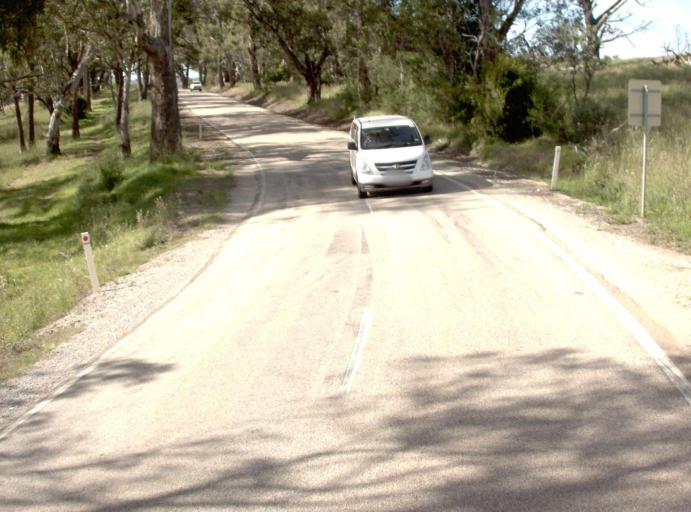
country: AU
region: Victoria
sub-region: East Gippsland
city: Lakes Entrance
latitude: -37.5187
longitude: 148.1619
